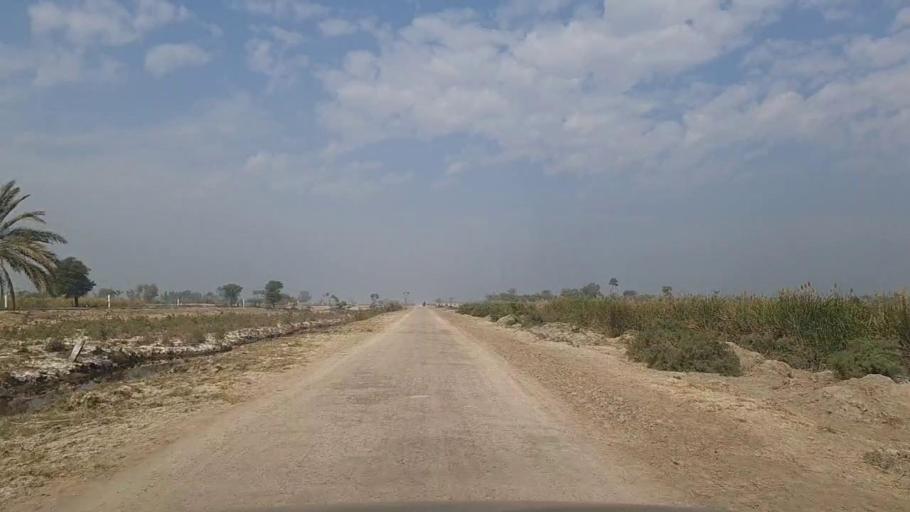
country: PK
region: Sindh
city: Daur
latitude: 26.3808
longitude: 68.3545
